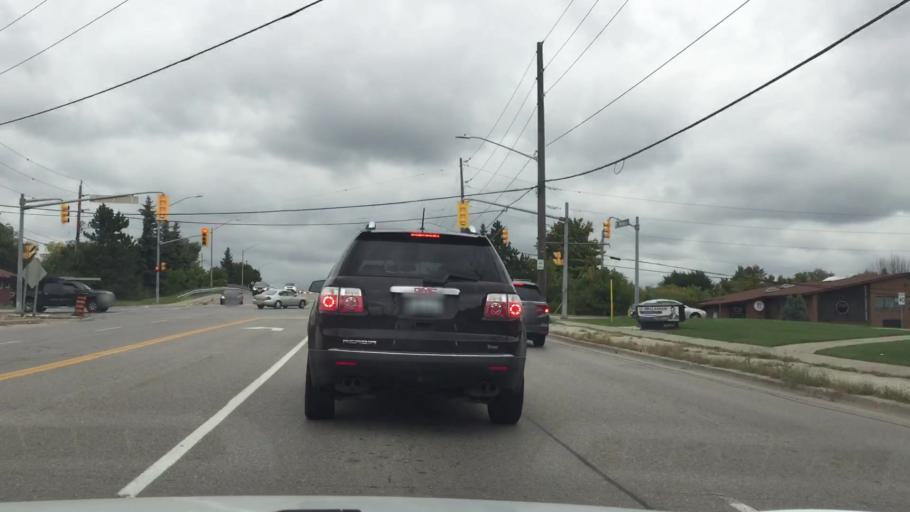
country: CA
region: Ontario
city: Pickering
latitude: 43.8217
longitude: -79.1166
